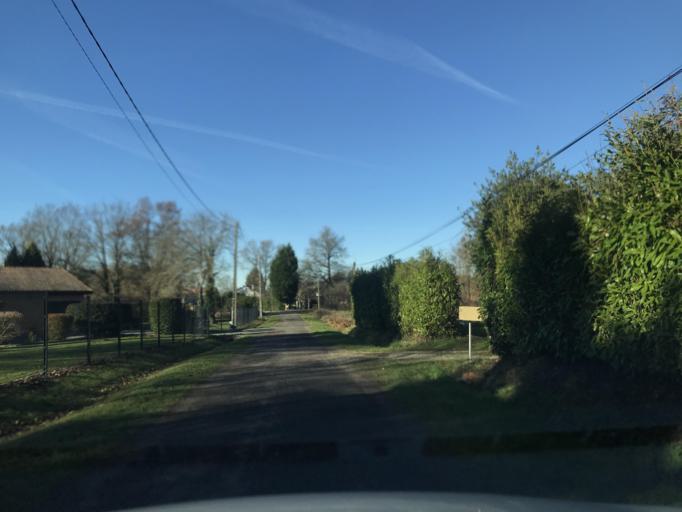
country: FR
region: Poitou-Charentes
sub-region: Departement de la Charente
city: Saint-Claud
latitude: 45.8559
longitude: 0.5154
